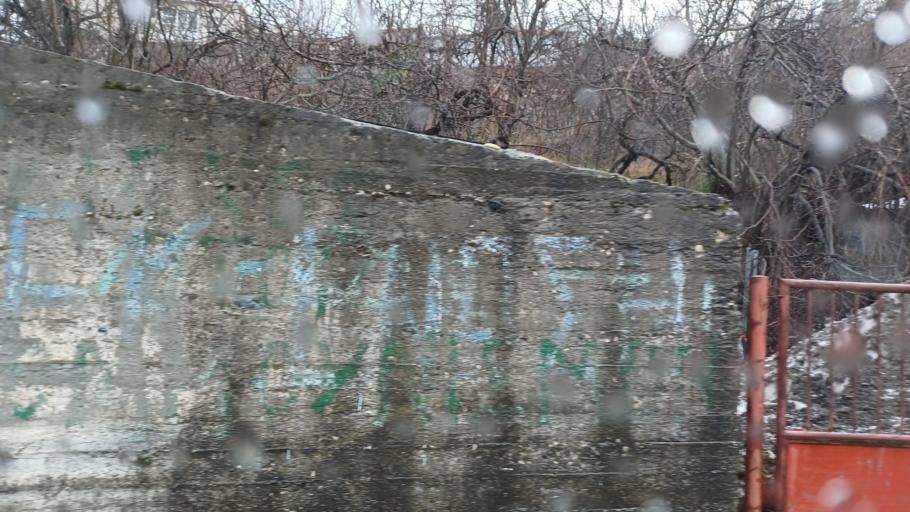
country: CY
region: Limassol
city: Kyperounta
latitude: 34.9378
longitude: 32.9739
